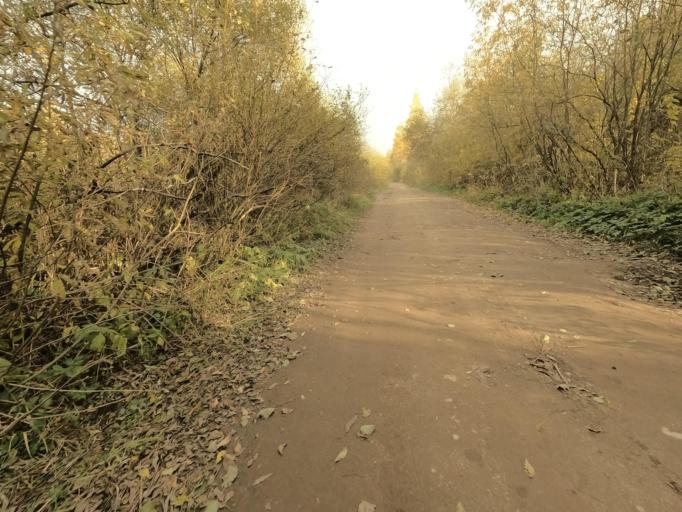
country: RU
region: Novgorod
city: Volkhovskiy
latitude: 58.8933
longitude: 31.0216
